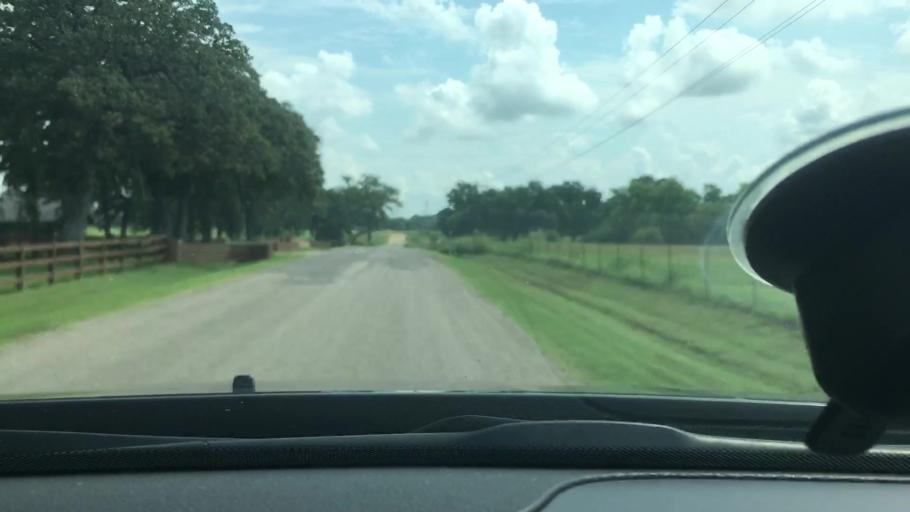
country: US
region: Oklahoma
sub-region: Carter County
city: Dickson
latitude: 34.2271
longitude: -96.8933
